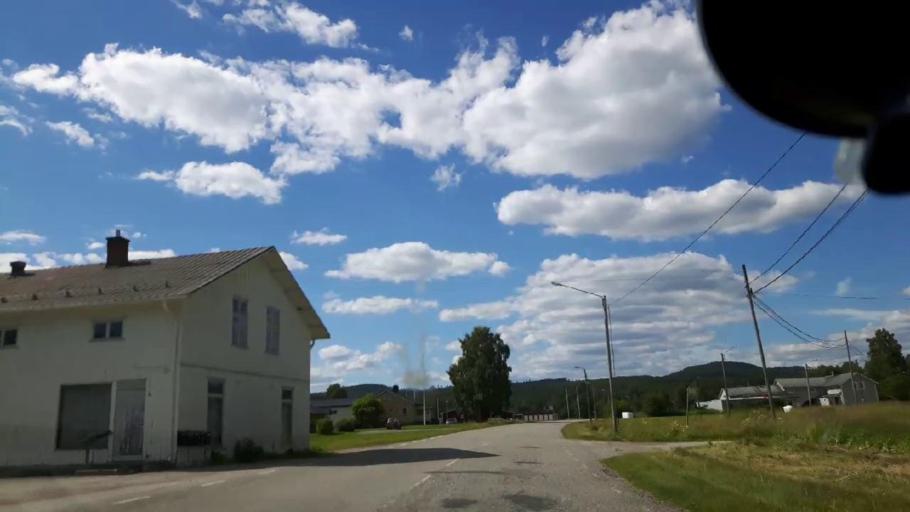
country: SE
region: Vaesternorrland
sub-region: Ange Kommun
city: Fransta
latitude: 62.7925
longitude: 16.2171
